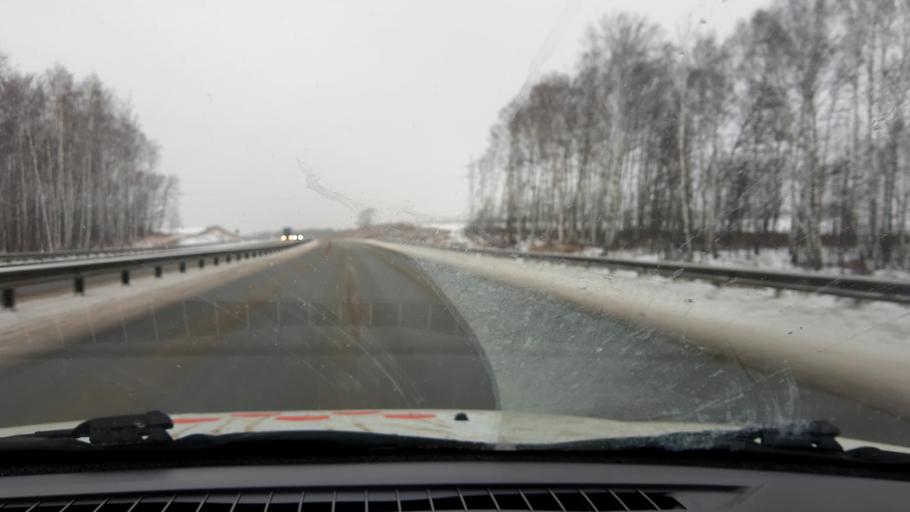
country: RU
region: Nizjnij Novgorod
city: Kstovo
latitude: 56.0994
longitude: 44.0574
